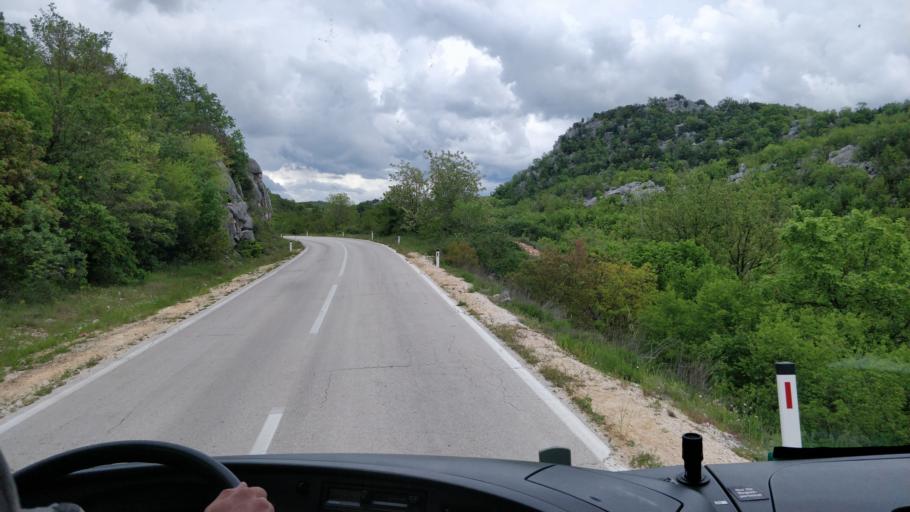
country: BA
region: Federation of Bosnia and Herzegovina
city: Ljubuski
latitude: 43.1738
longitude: 17.4930
